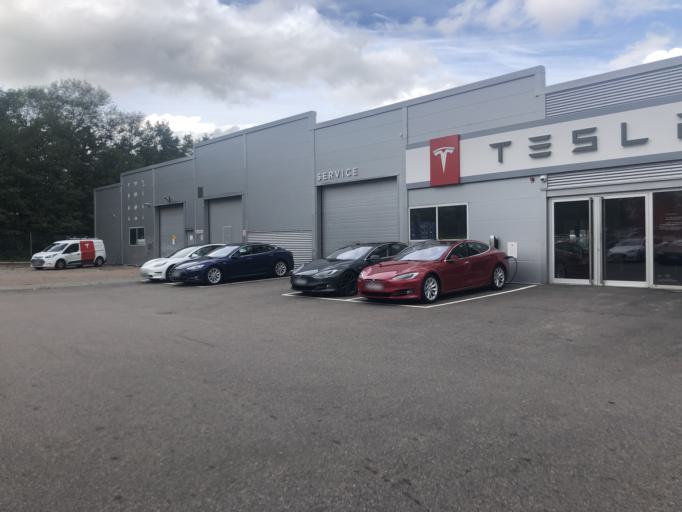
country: SE
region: Vaestra Goetaland
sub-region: Molndal
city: Moelndal
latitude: 57.6426
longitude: 11.9944
